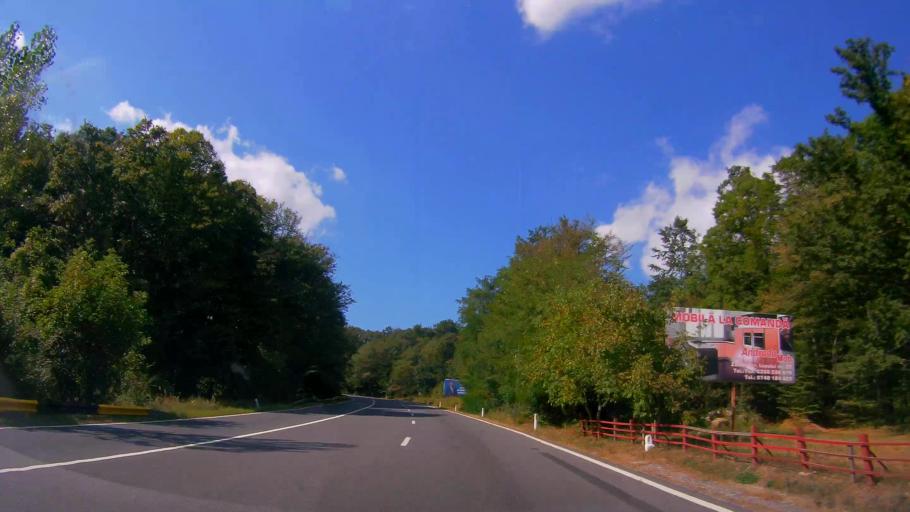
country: RO
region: Salaj
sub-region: Comuna Treznea
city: Treznea
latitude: 47.1419
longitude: 23.1142
